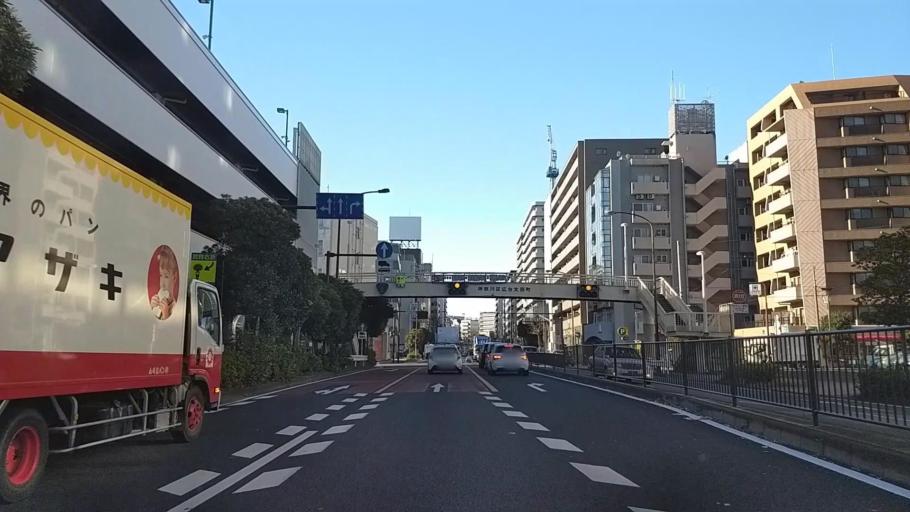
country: JP
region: Kanagawa
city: Yokohama
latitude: 35.4780
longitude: 139.6295
